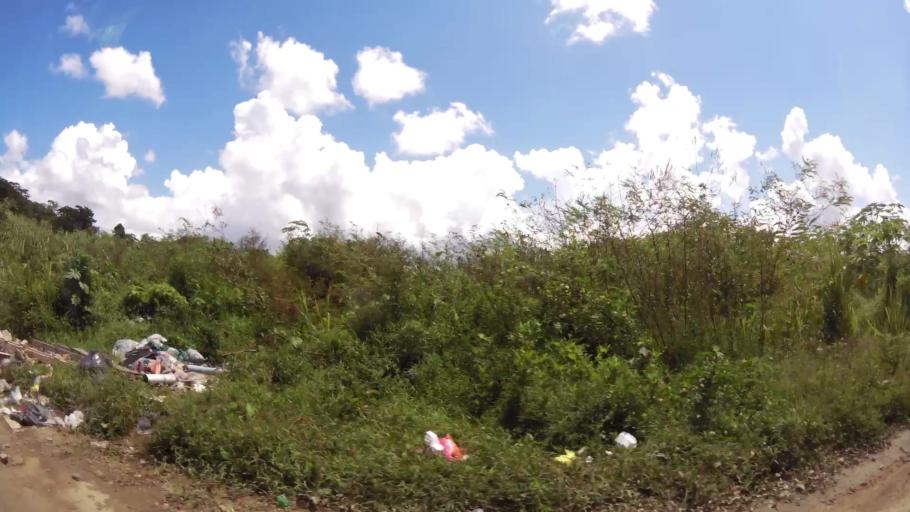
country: SR
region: Paramaribo
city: Paramaribo
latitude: 5.8603
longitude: -55.1506
